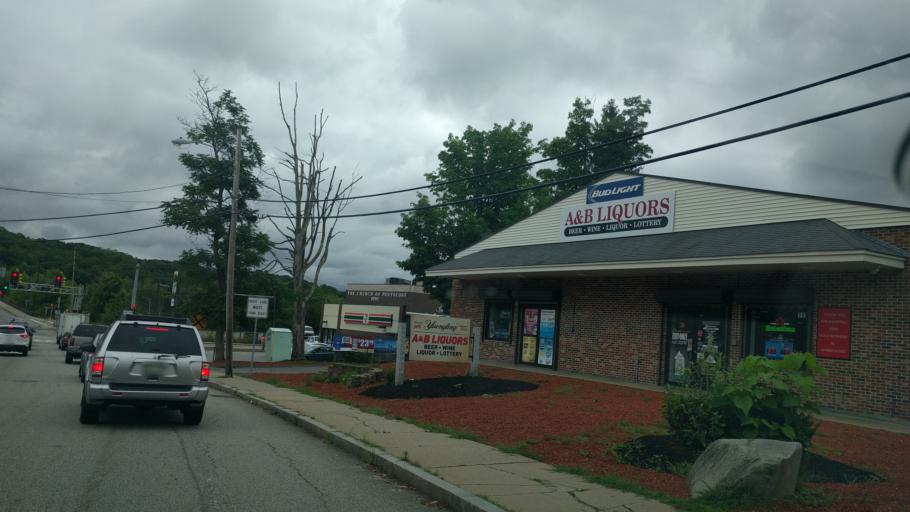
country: US
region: Massachusetts
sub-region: Worcester County
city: Sunderland
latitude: 42.2351
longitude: -71.7974
